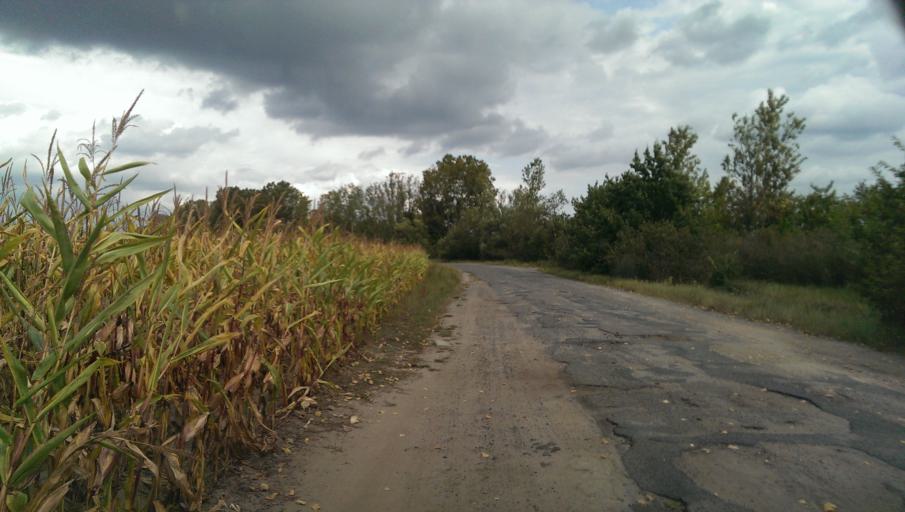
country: DE
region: Brandenburg
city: Rangsdorf
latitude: 52.2943
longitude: 13.4763
